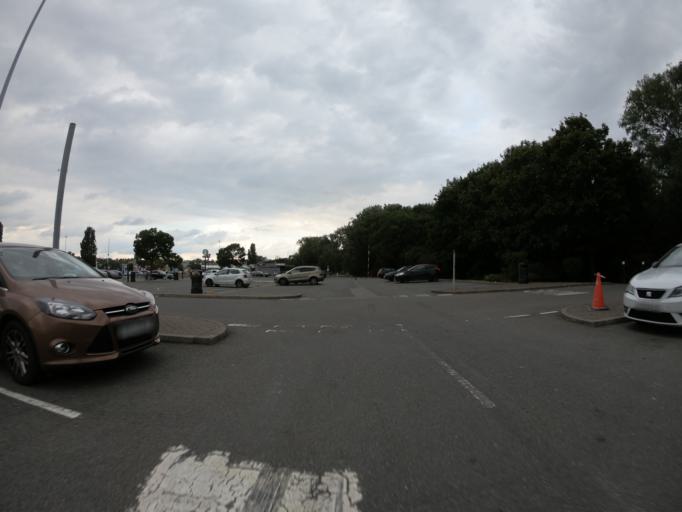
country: GB
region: England
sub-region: Greater London
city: Barking
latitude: 51.5205
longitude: 0.0724
